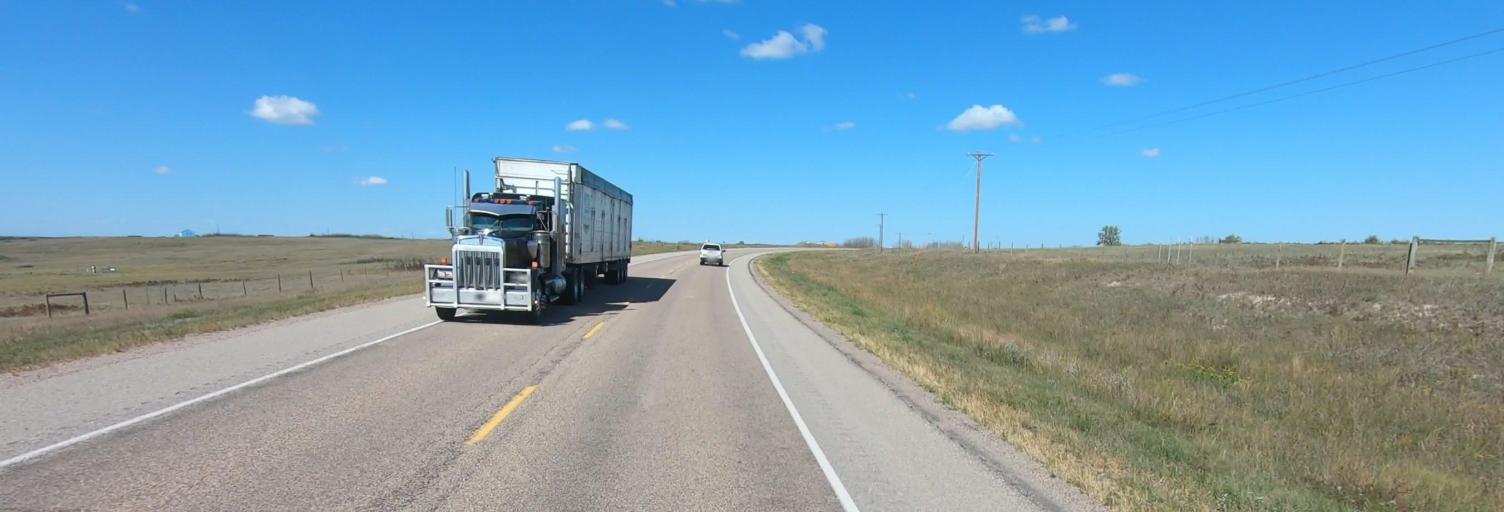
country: CA
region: Alberta
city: Strathmore
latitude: 50.8724
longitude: -113.1607
